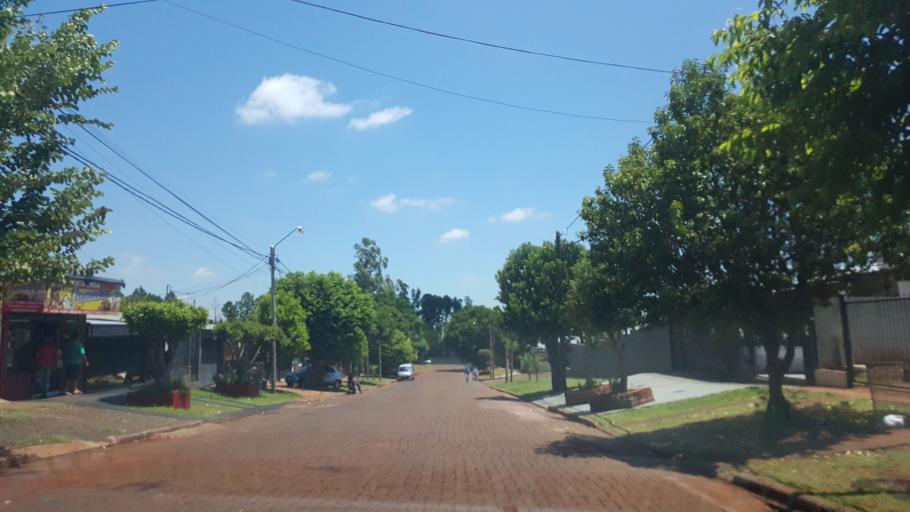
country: AR
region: Misiones
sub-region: Departamento de Capital
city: Posadas
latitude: -27.4176
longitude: -55.9543
